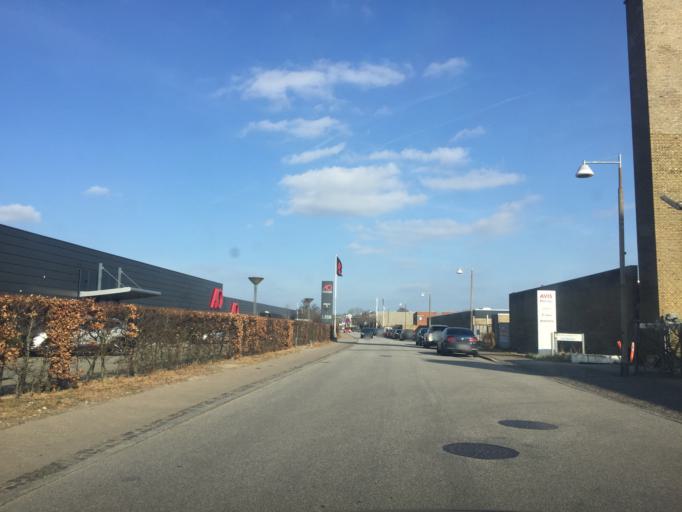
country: DK
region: Capital Region
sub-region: Albertslund Kommune
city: Albertslund
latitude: 55.6653
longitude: 12.3631
